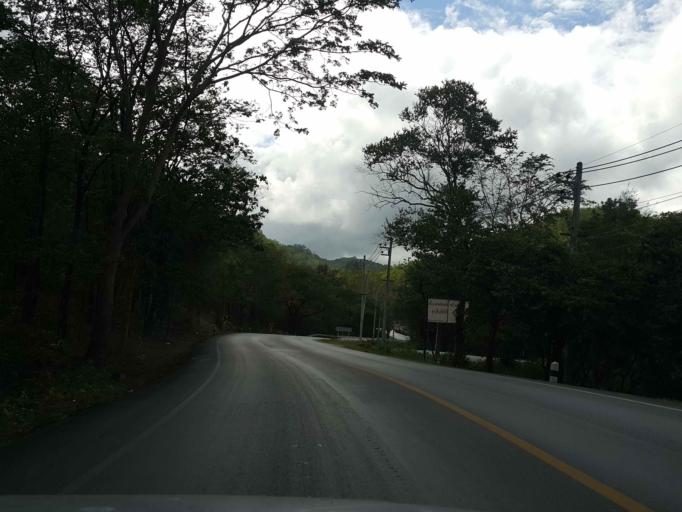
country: TH
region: Tak
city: Tak
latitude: 16.8095
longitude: 98.9895
